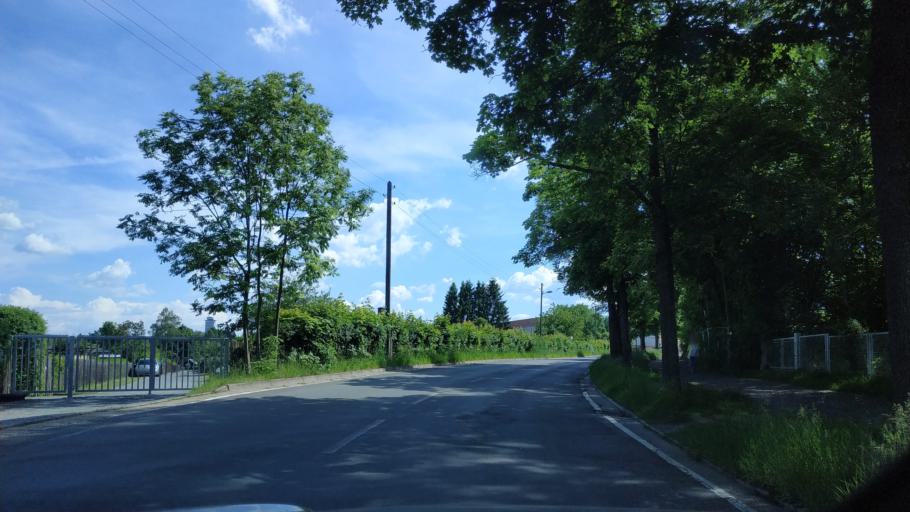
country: DE
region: Saxony
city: Plauen
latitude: 50.5171
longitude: 12.1326
